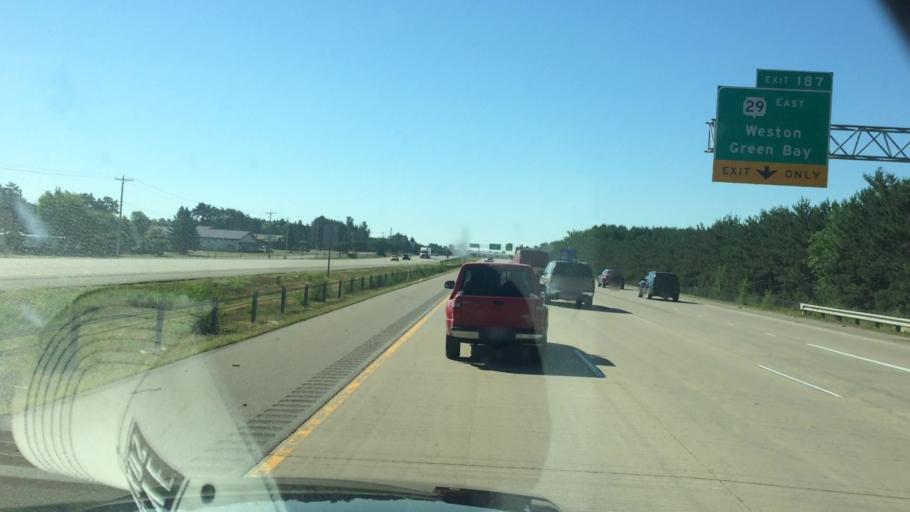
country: US
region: Wisconsin
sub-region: Marathon County
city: Rib Mountain
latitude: 44.9076
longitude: -89.6481
